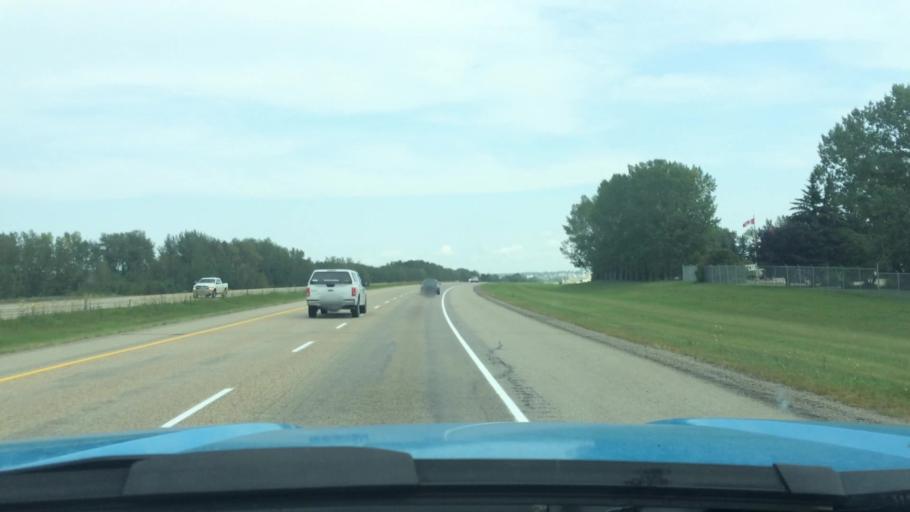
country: CA
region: Alberta
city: Penhold
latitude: 51.9791
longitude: -113.9949
